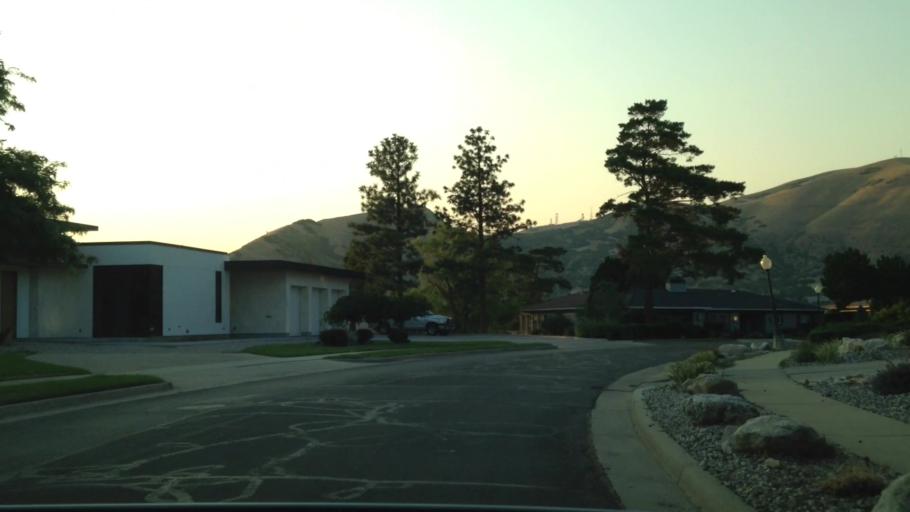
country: US
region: Utah
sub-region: Salt Lake County
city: Salt Lake City
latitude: 40.7874
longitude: -111.8762
